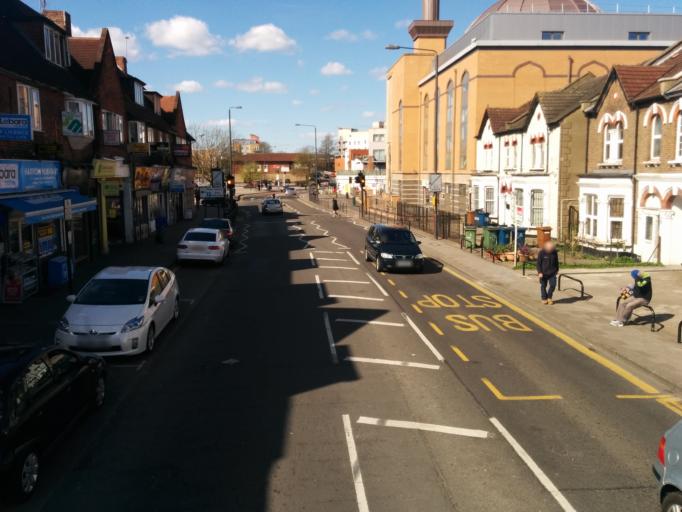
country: GB
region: England
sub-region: Greater London
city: Greenhill
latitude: 51.5884
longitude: -0.3324
